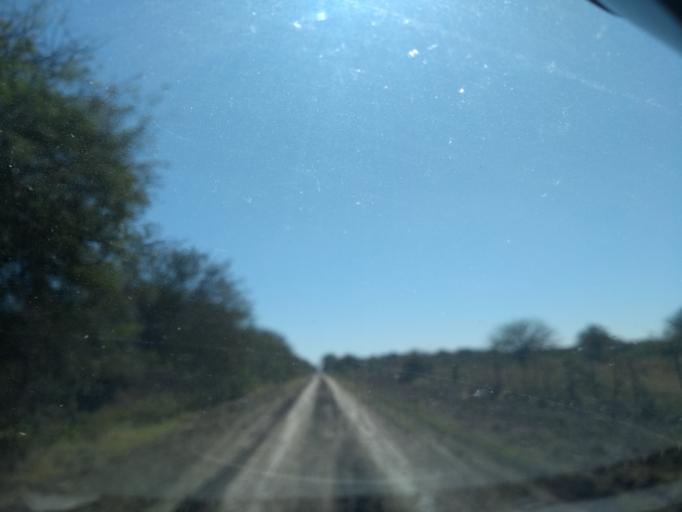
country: AR
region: Chaco
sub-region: Departamento de Quitilipi
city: Quitilipi
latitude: -26.7334
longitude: -60.2328
